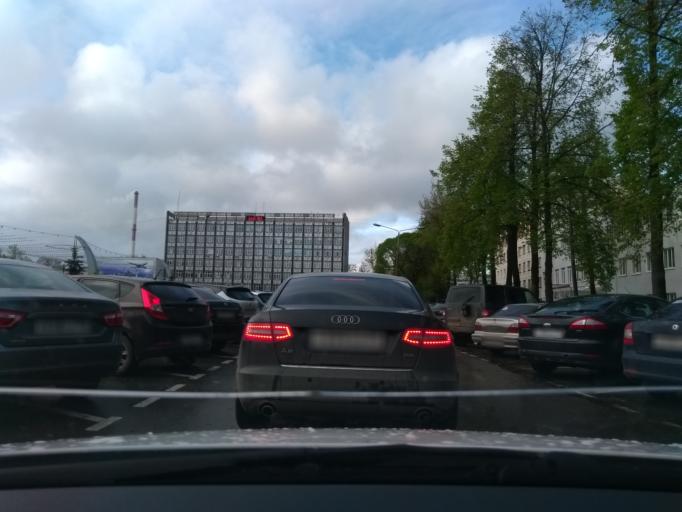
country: RU
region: Perm
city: Perm
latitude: 57.9841
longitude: 56.2528
